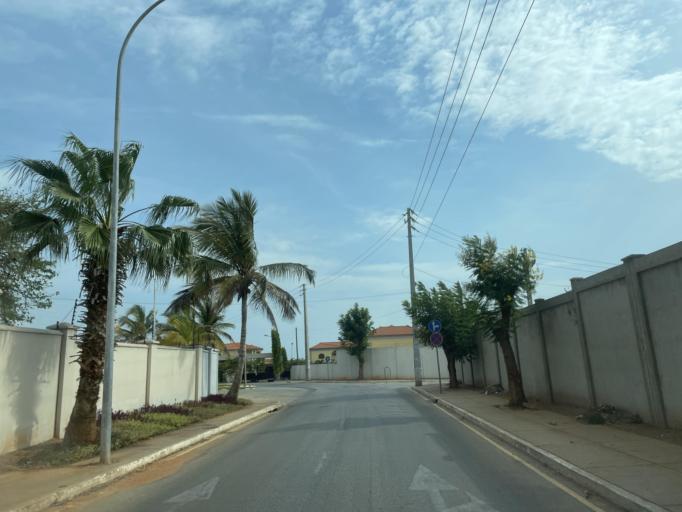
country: AO
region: Luanda
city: Luanda
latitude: -8.9279
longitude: 13.1784
